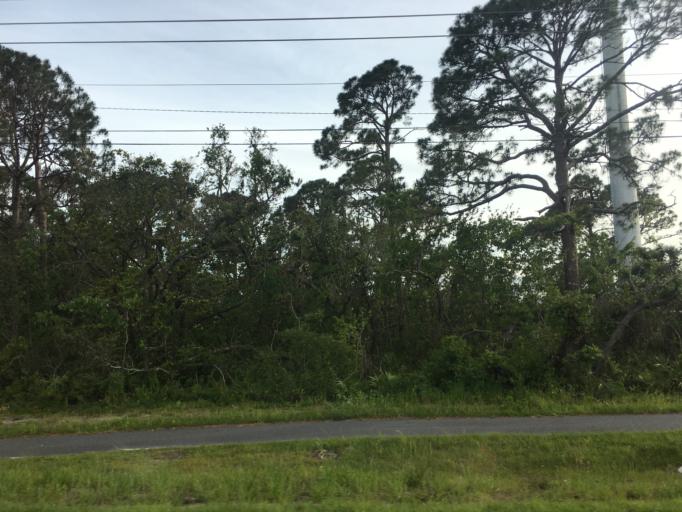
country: US
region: Florida
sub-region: Bay County
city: Panama City Beach
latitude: 30.1735
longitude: -85.7931
